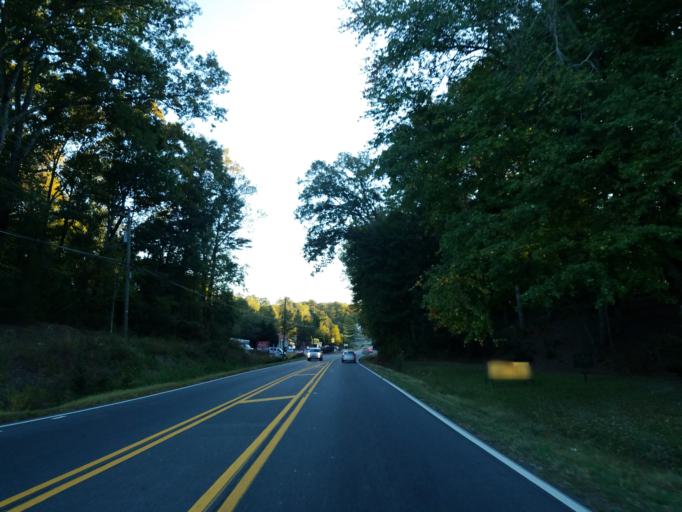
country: US
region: Georgia
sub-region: Forsyth County
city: Cumming
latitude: 34.2311
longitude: -84.1252
